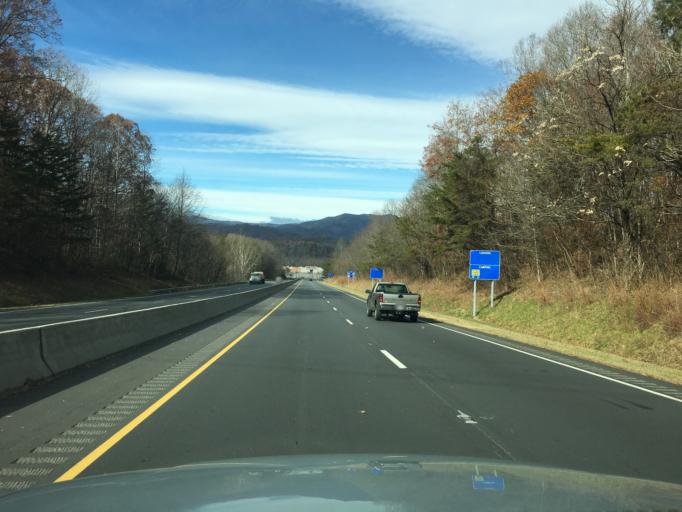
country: US
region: North Carolina
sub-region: McDowell County
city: Marion
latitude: 35.6990
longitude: -82.0314
